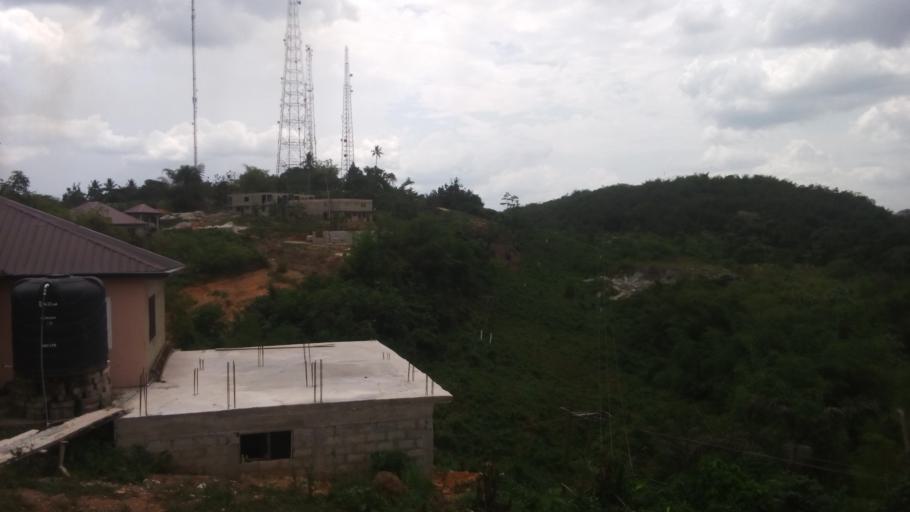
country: GH
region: Western
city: Tarkwa
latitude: 5.3055
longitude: -2.0057
